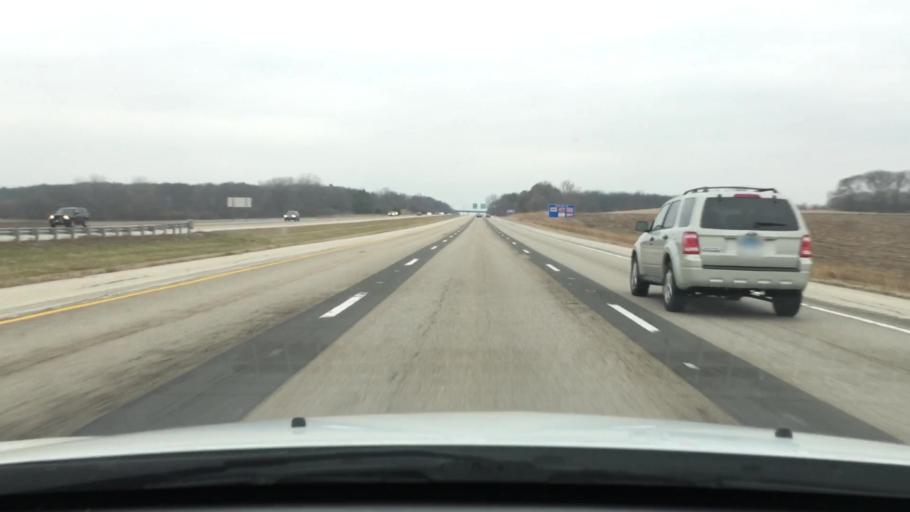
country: US
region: Illinois
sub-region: Logan County
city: Lincoln
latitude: 40.1357
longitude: -89.4169
